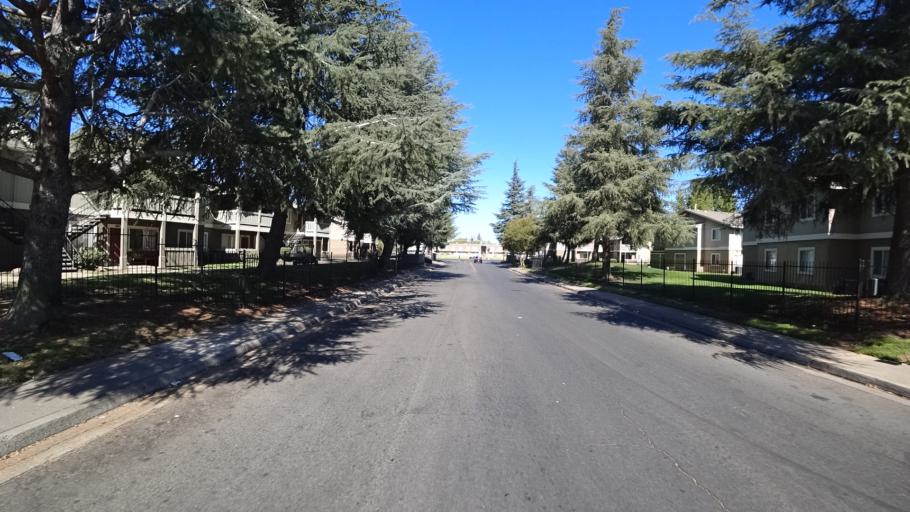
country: US
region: California
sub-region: Sacramento County
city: Parkway
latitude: 38.4733
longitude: -121.4417
